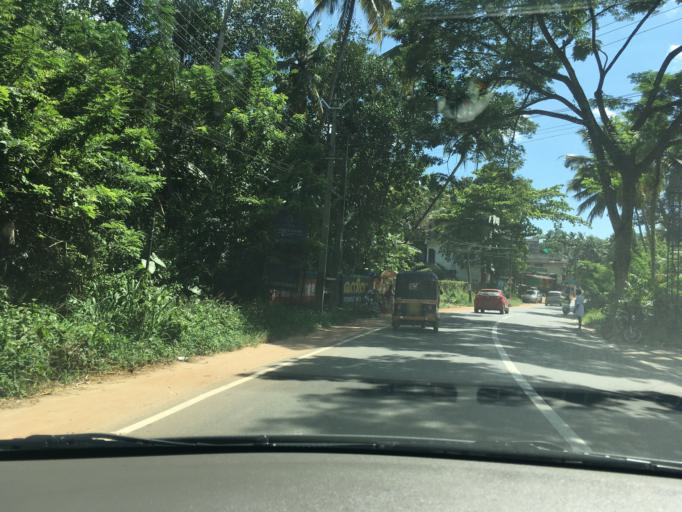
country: IN
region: Kerala
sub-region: Thiruvananthapuram
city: Nedumangad
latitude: 8.5780
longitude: 76.9964
